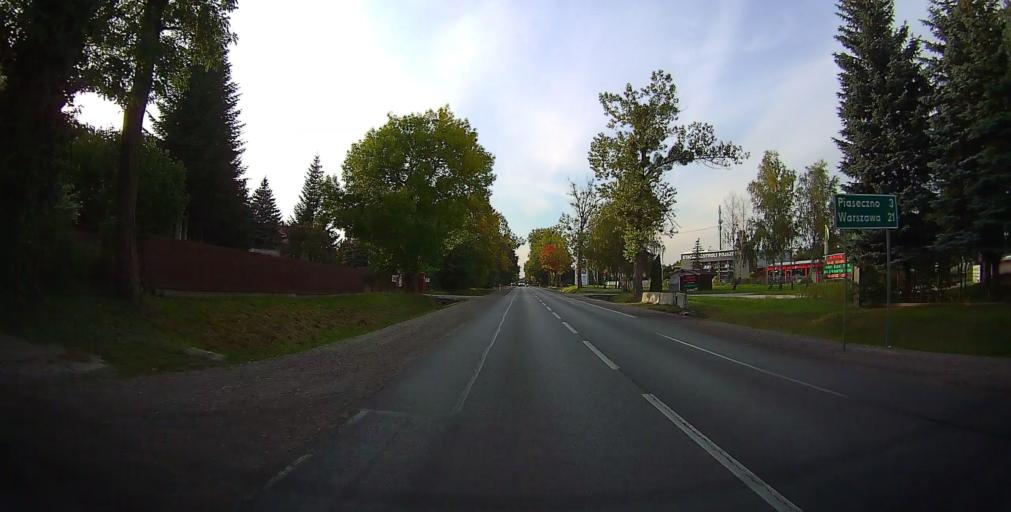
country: PL
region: Masovian Voivodeship
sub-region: Powiat piaseczynski
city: Zabieniec
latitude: 52.0532
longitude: 21.0596
